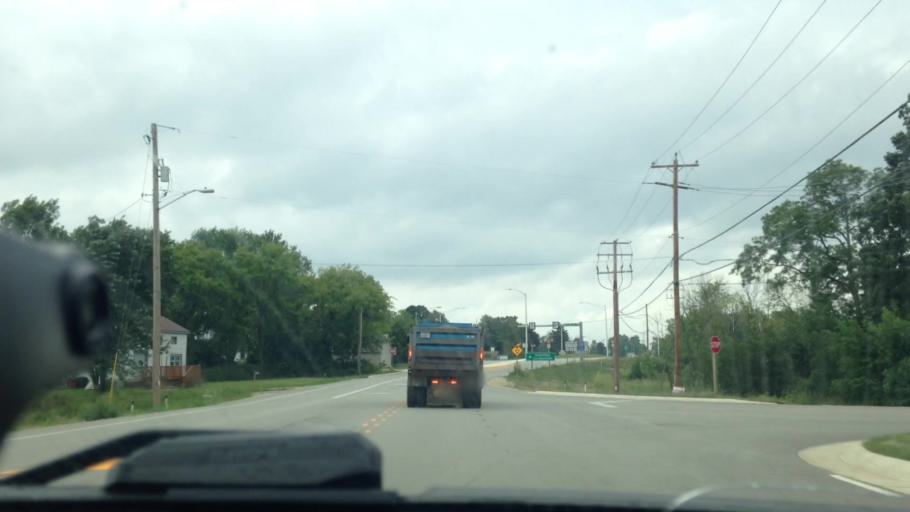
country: US
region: Wisconsin
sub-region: Waukesha County
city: Menomonee Falls
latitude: 43.2073
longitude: -88.1594
